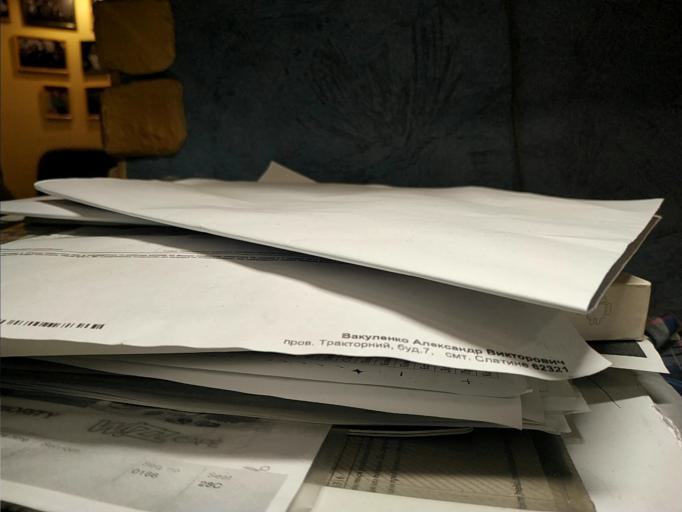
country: RU
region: Tverskaya
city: Zubtsov
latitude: 56.0951
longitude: 34.7173
